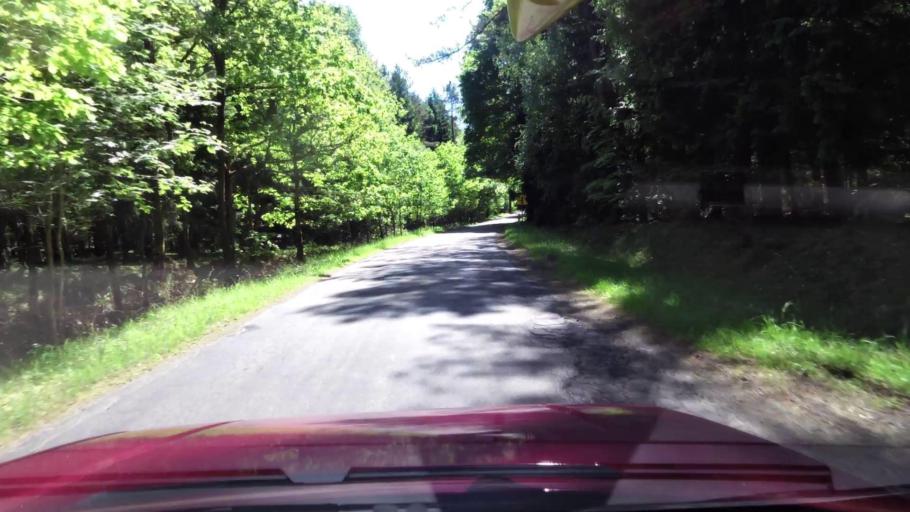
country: PL
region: West Pomeranian Voivodeship
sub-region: Powiat koszalinski
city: Bobolice
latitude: 54.0783
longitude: 16.4928
